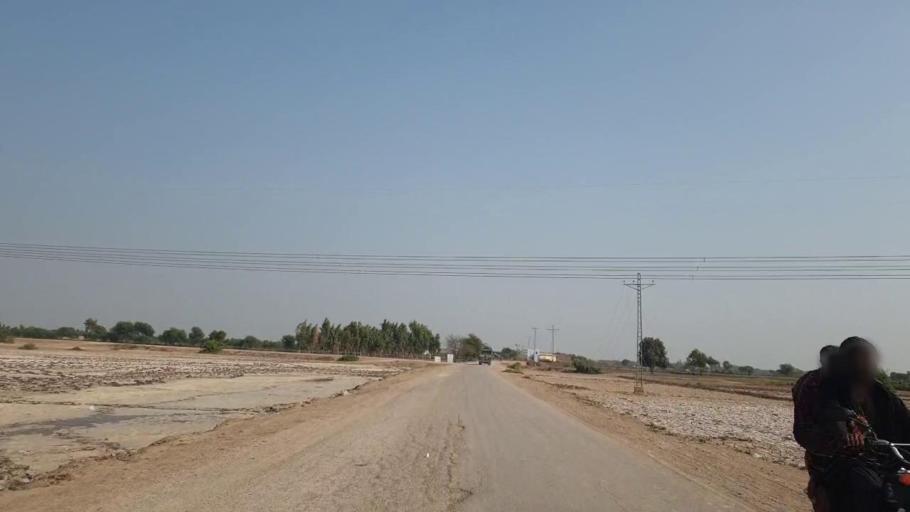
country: PK
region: Sindh
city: Matiari
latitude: 25.5019
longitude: 68.4546
